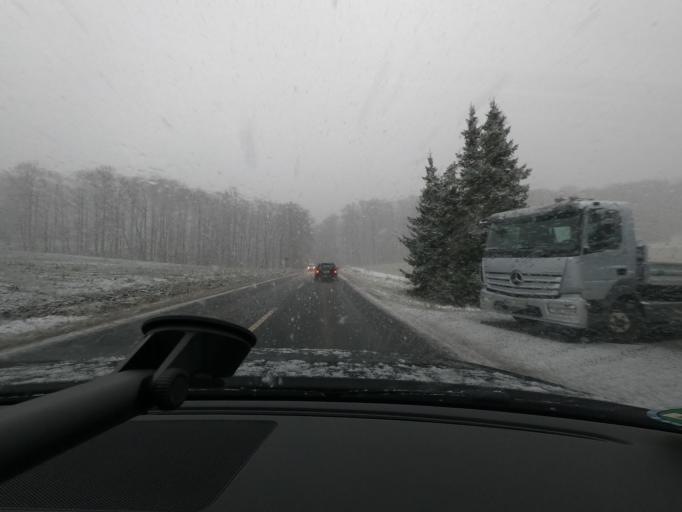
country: DE
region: Thuringia
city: Kallmerode
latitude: 51.3445
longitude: 10.3118
